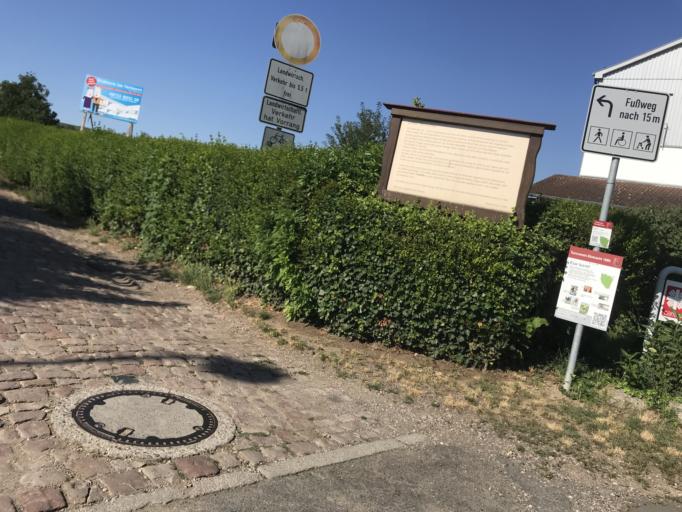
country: DE
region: Rheinland-Pfalz
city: Gau-Algesheim
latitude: 49.9555
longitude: 8.0117
